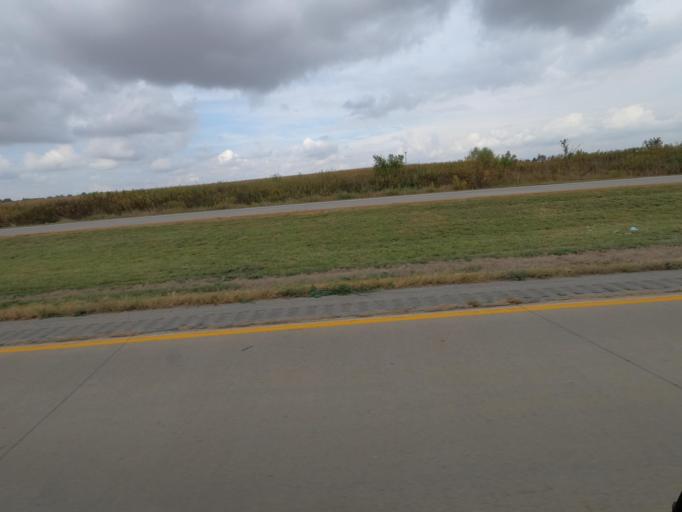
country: US
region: Iowa
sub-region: Jasper County
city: Prairie City
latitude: 41.5880
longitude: -93.2197
